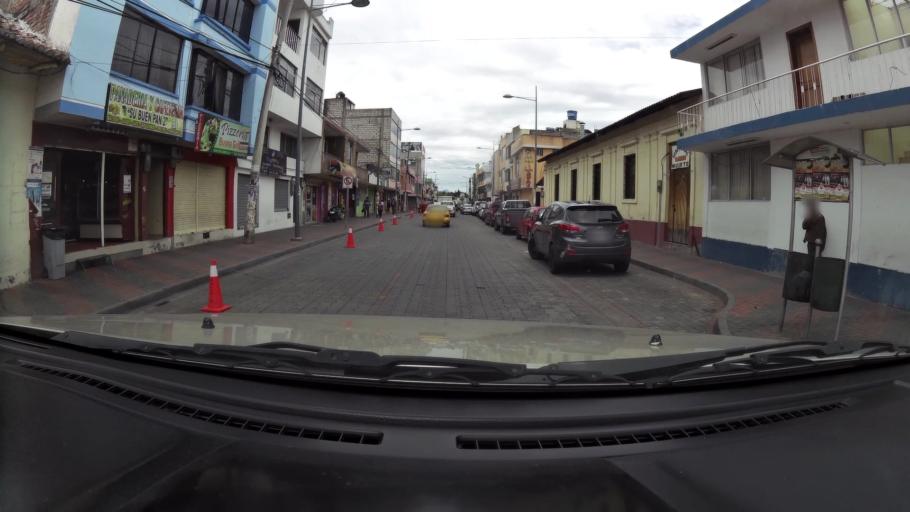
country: EC
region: Cotopaxi
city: San Miguel de Salcedo
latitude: -1.0262
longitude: -78.5913
